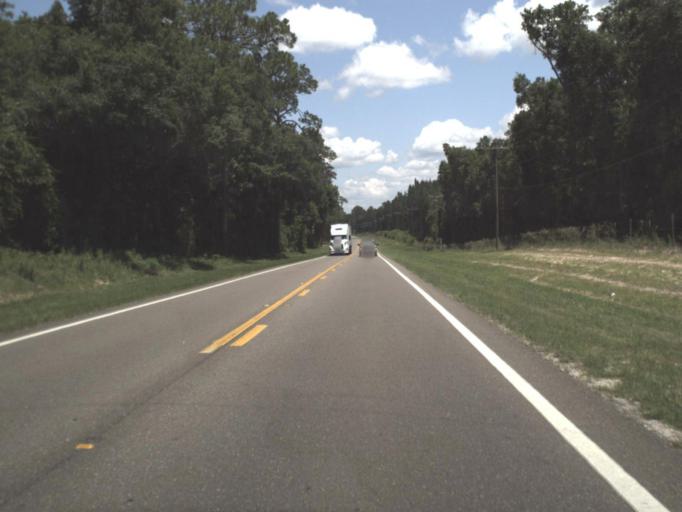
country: US
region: Florida
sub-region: Clay County
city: Keystone Heights
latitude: 29.7306
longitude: -82.0481
